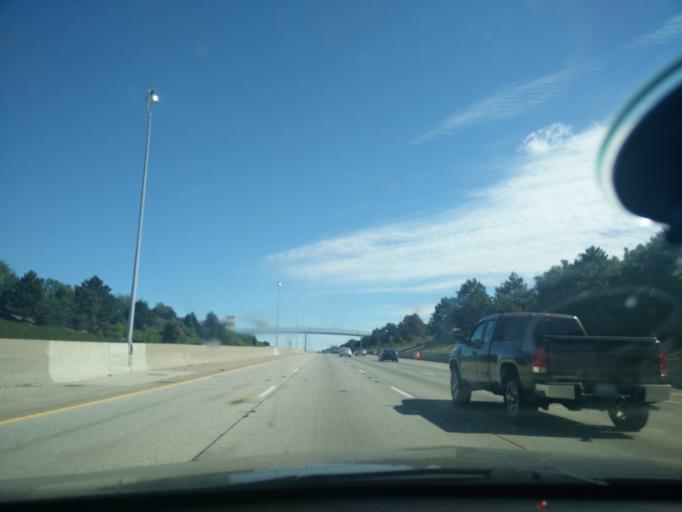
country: US
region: Michigan
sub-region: Macomb County
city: Roseville
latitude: 42.4940
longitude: -82.9596
